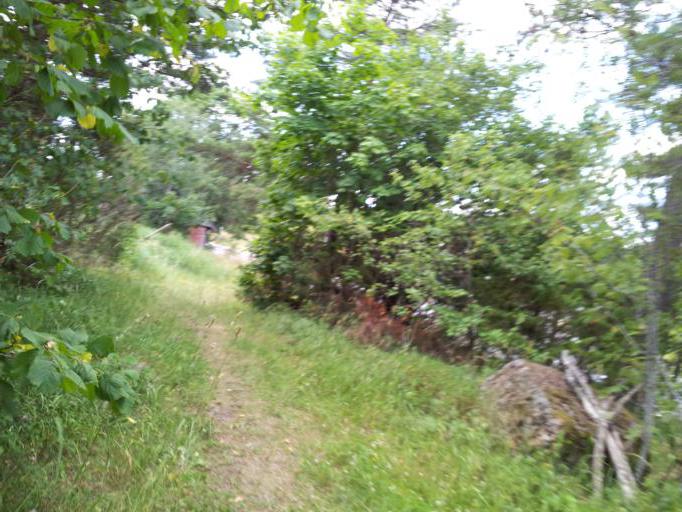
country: SE
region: Stockholm
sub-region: Norrtalje Kommun
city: Nykvarn
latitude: 59.9047
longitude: 18.2584
